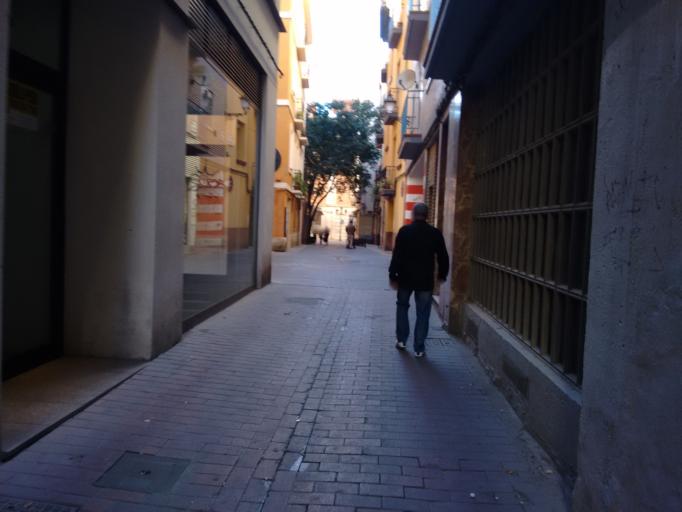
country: ES
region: Aragon
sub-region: Provincia de Zaragoza
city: Zaragoza
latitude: 41.6519
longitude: -0.8750
